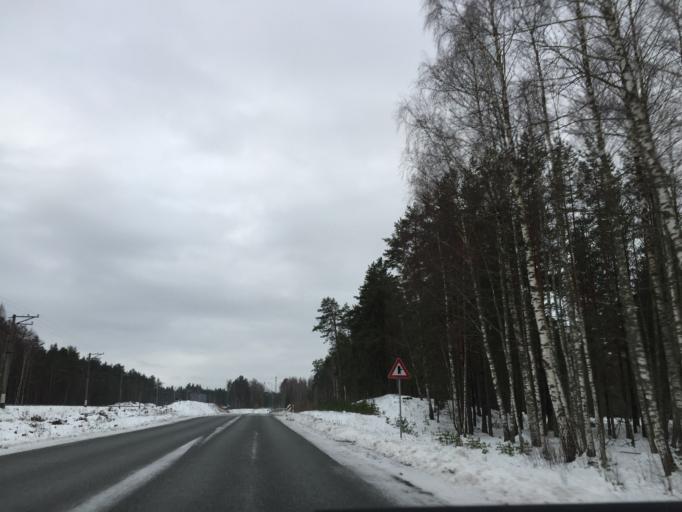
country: LV
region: Saulkrastu
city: Saulkrasti
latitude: 57.2001
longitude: 24.3683
